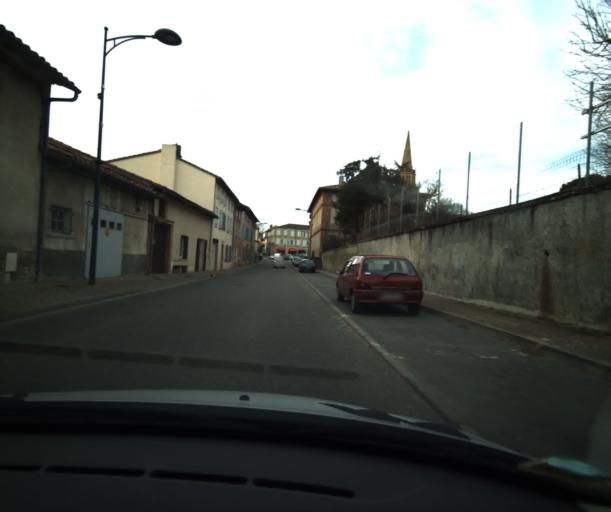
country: FR
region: Midi-Pyrenees
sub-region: Departement du Tarn-et-Garonne
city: Montech
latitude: 43.9555
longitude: 1.2309
